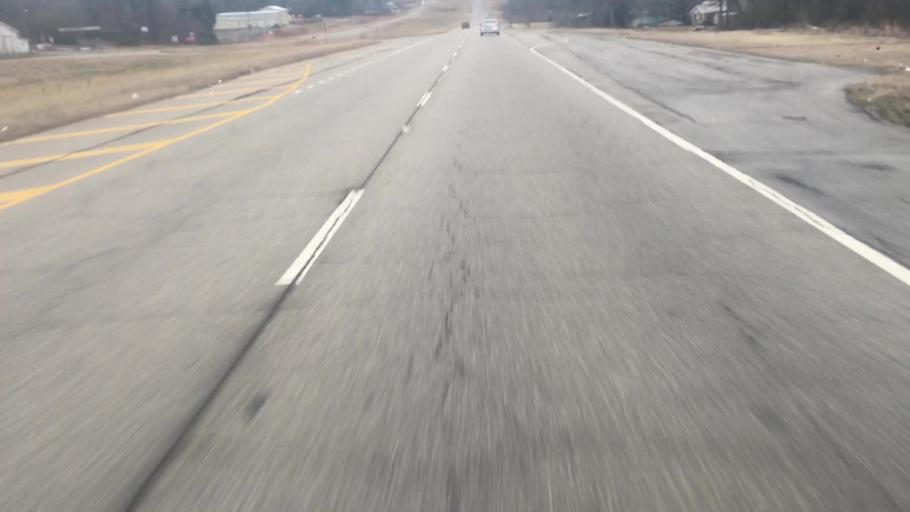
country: US
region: Alabama
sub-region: Walker County
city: Cordova
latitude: 33.8059
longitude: -87.1378
